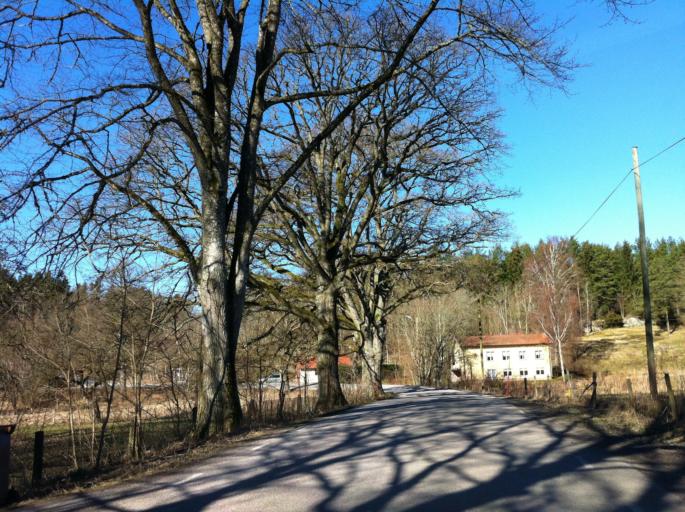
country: SE
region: Vaestra Goetaland
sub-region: Grastorps Kommun
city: Graestorp
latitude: 58.4324
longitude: 12.6109
